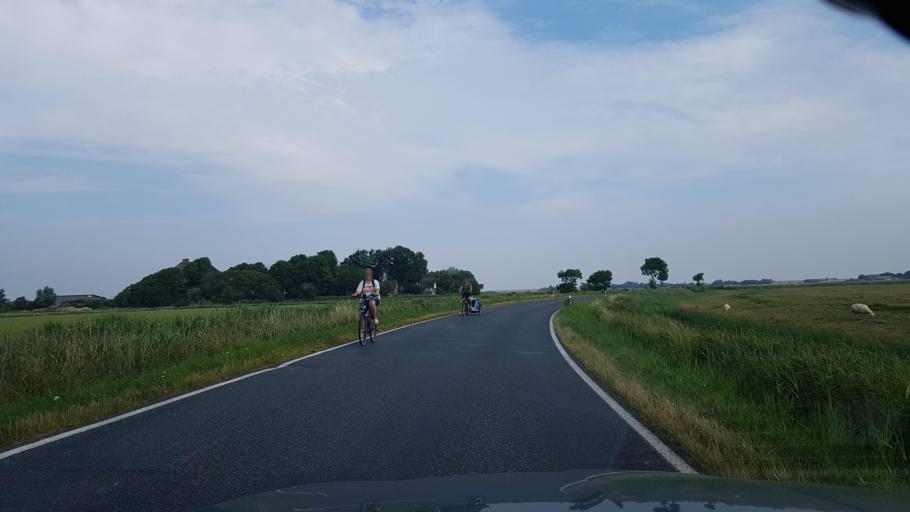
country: DE
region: Schleswig-Holstein
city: Westerhever
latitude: 54.3762
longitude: 8.6893
